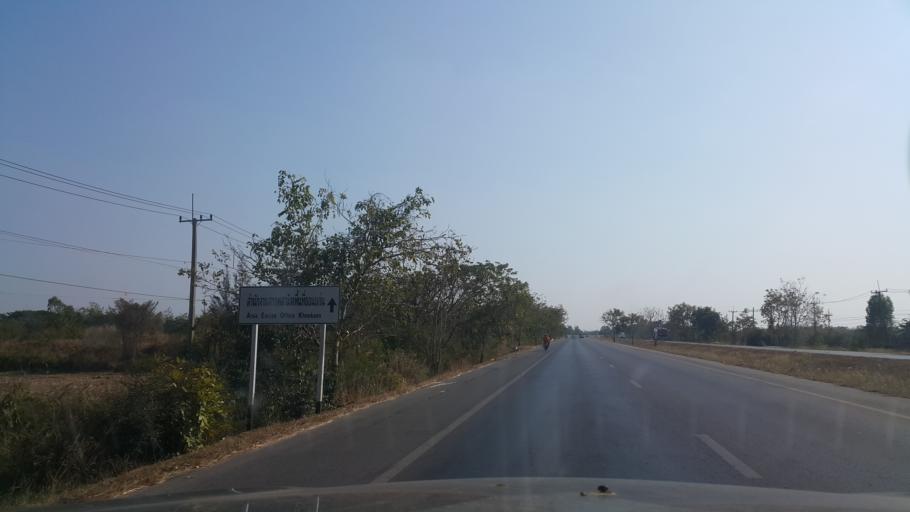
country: TH
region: Khon Kaen
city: Khon Kaen
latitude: 16.4293
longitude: 102.9174
